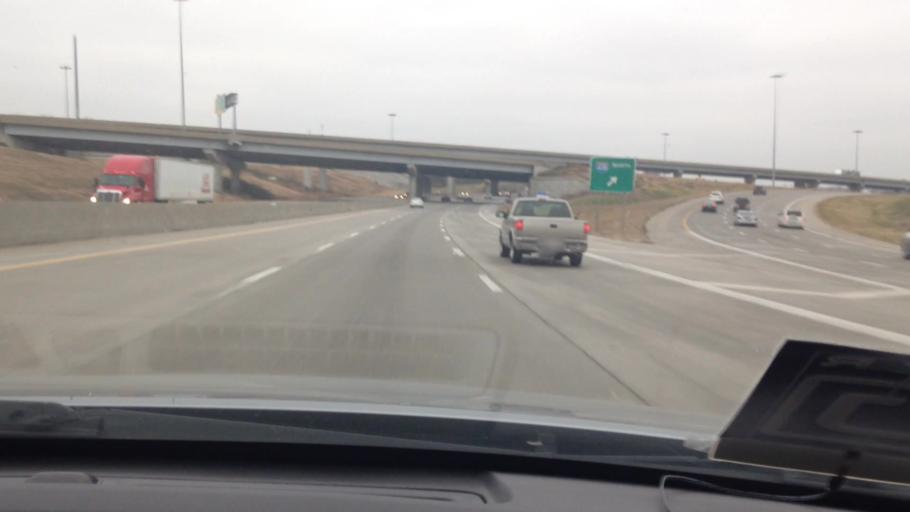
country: US
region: Missouri
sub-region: Jackson County
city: Grandview
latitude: 38.9394
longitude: -94.5356
